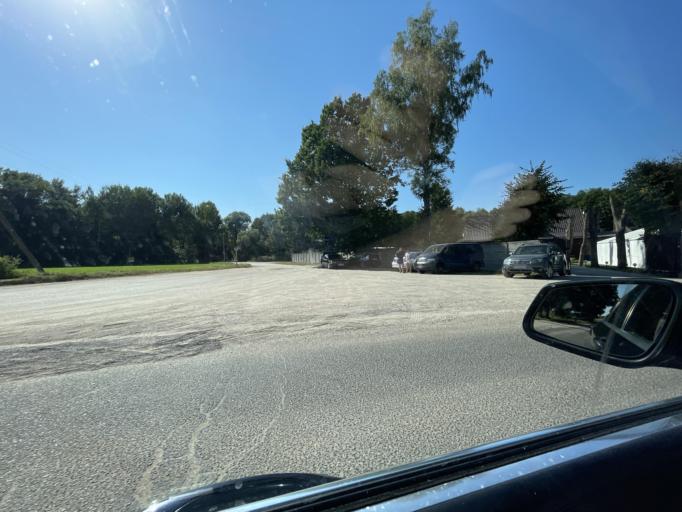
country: BY
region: Grodnenskaya
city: Hrodna
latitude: 53.7456
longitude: 23.9740
